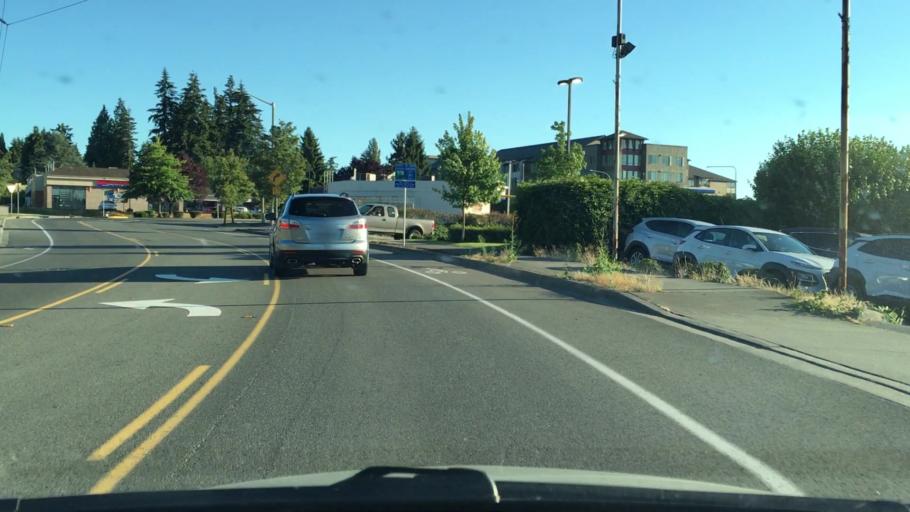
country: US
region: Washington
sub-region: King County
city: Kingsgate
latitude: 47.7050
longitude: -122.1747
